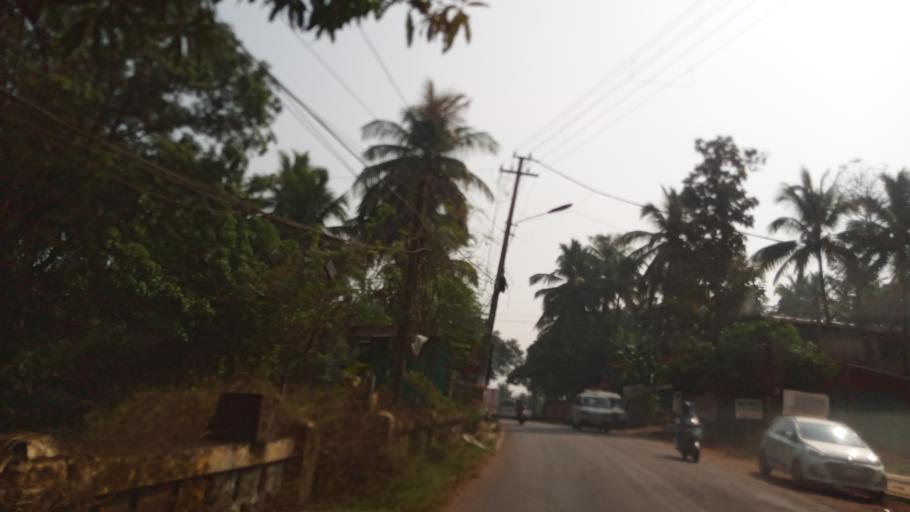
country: IN
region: Goa
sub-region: North Goa
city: Saligao
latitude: 15.5463
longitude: 73.7989
